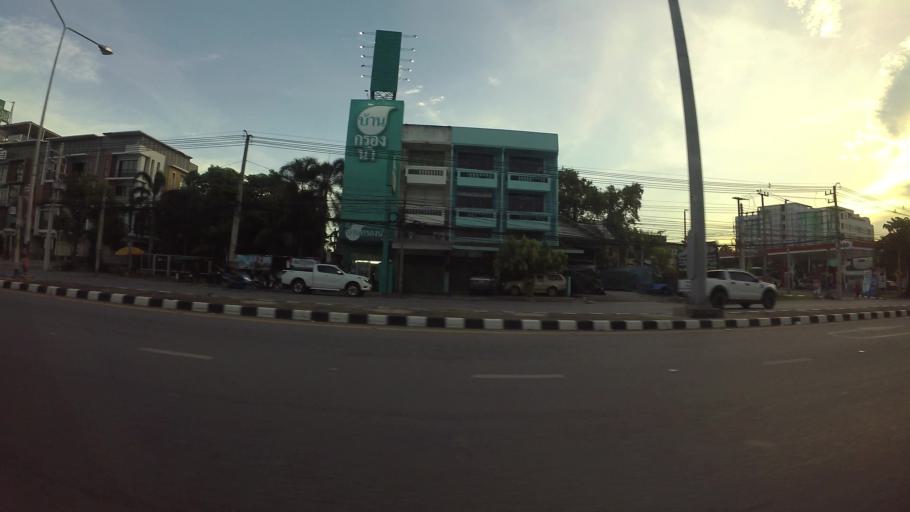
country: TH
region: Rayong
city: Rayong
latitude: 12.6793
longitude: 101.2857
